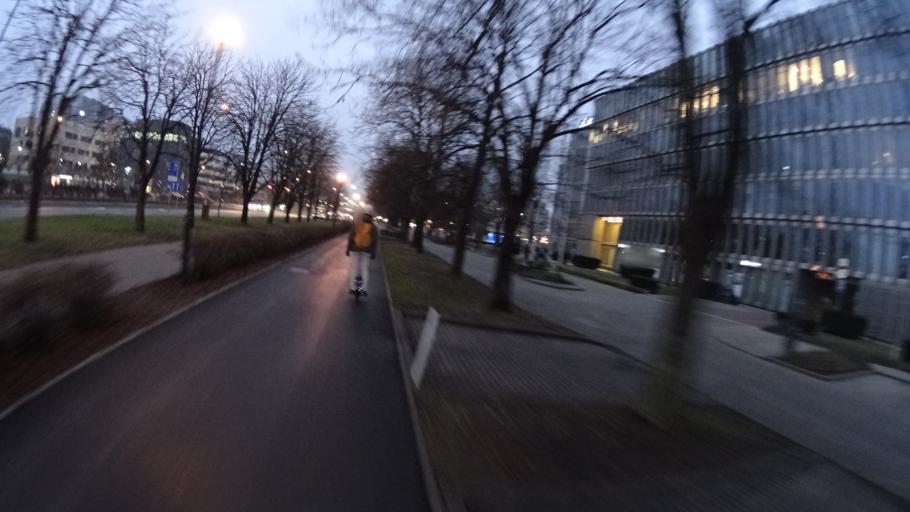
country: PL
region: Masovian Voivodeship
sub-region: Warszawa
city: Mokotow
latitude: 52.1846
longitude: 21.0016
